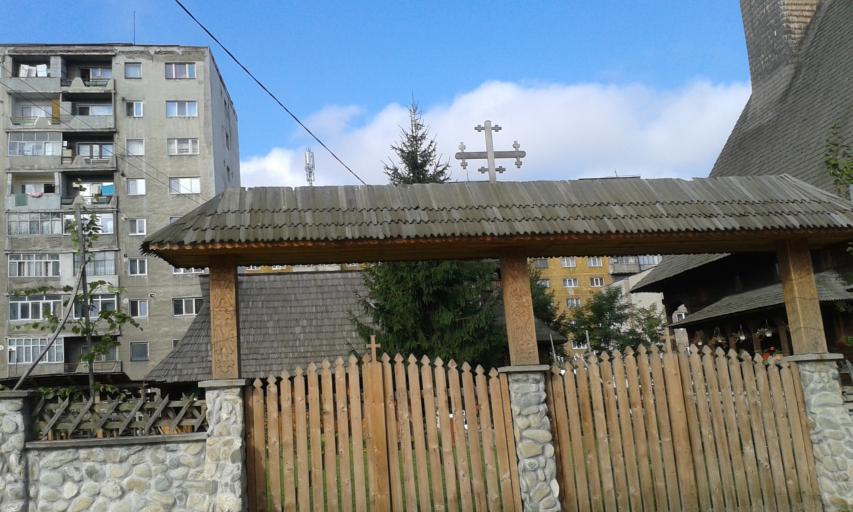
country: RO
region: Hunedoara
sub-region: Municipiul Petrosani
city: Petrosani
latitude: 45.3925
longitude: 23.3766
